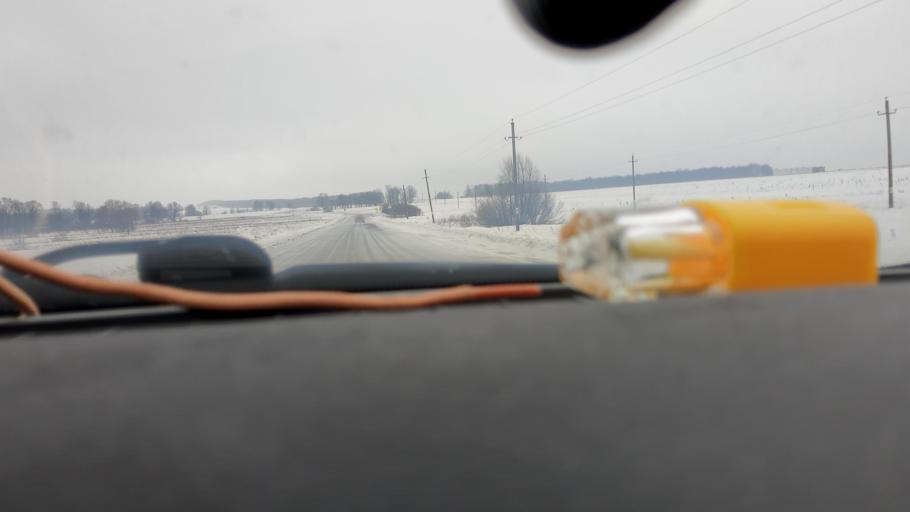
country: RU
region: Bashkortostan
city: Ulukulevo
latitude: 54.5945
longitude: 56.4264
